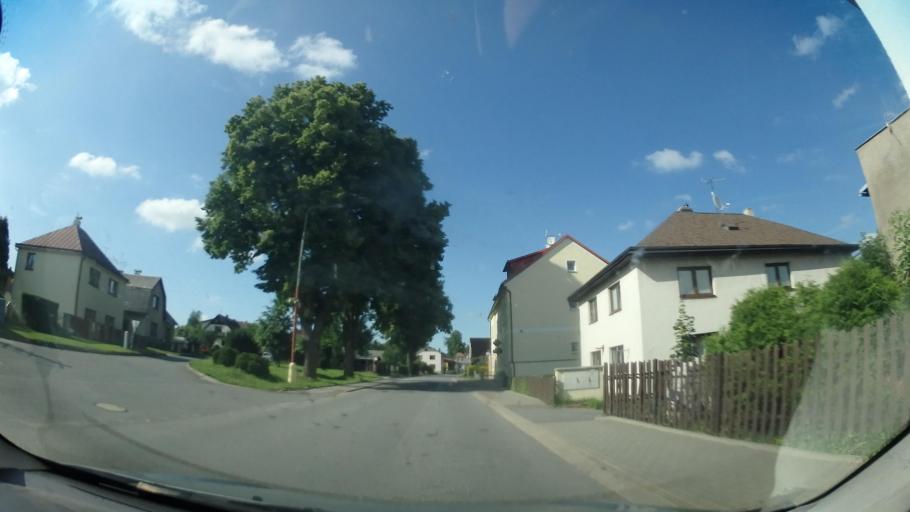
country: CZ
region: Vysocina
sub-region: Okres Zd'ar nad Sazavou
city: Svratka
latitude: 49.7199
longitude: 16.0352
